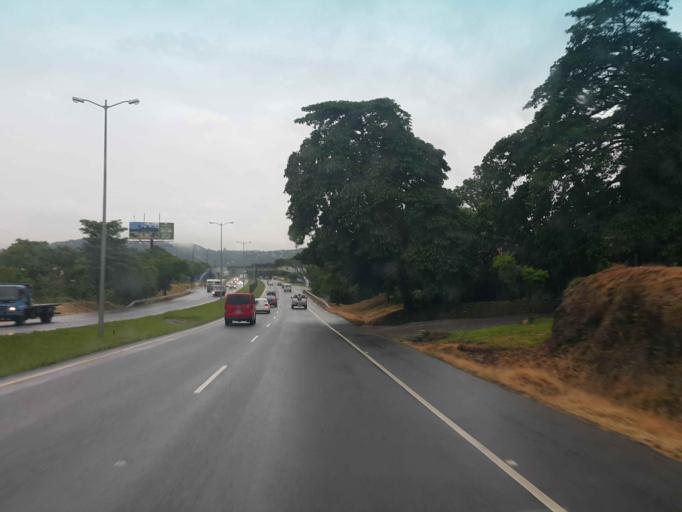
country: CR
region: San Jose
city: Santa Ana
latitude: 9.9380
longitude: -84.2076
